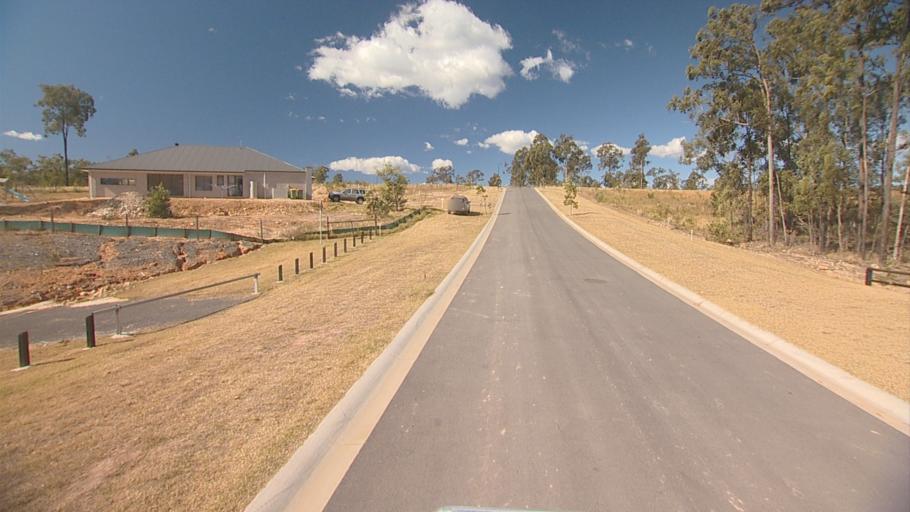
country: AU
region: Queensland
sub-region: Logan
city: North Maclean
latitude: -27.7593
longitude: 152.9301
